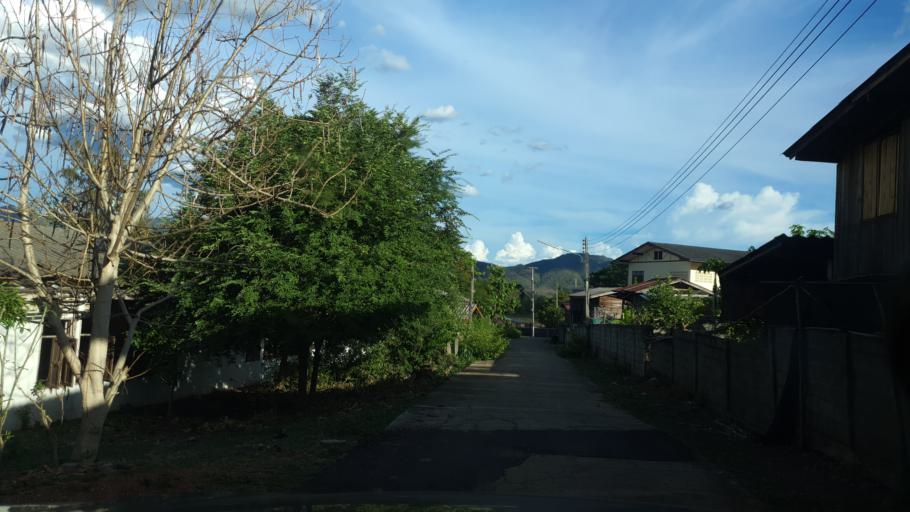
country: TH
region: Lampang
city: Sop Prap
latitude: 17.8771
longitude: 99.2981
